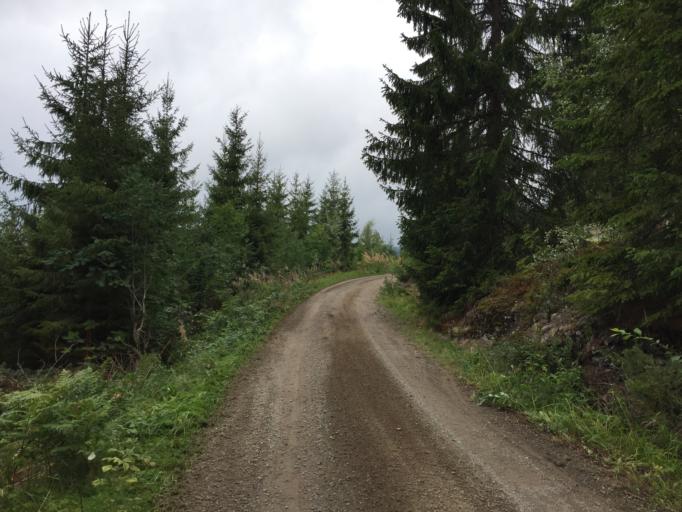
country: NO
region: Akershus
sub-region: Baerum
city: Sandvika
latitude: 60.0190
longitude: 10.5546
